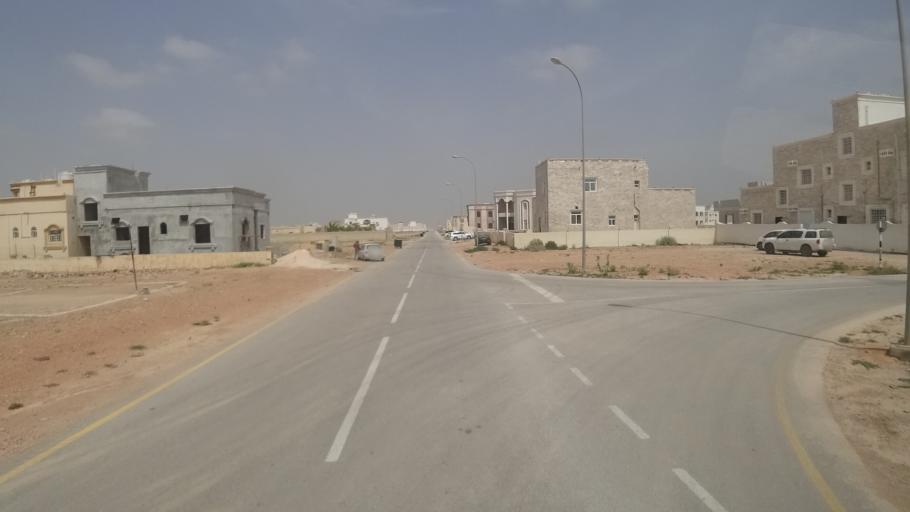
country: OM
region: Zufar
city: Salalah
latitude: 17.1000
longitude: 54.2147
